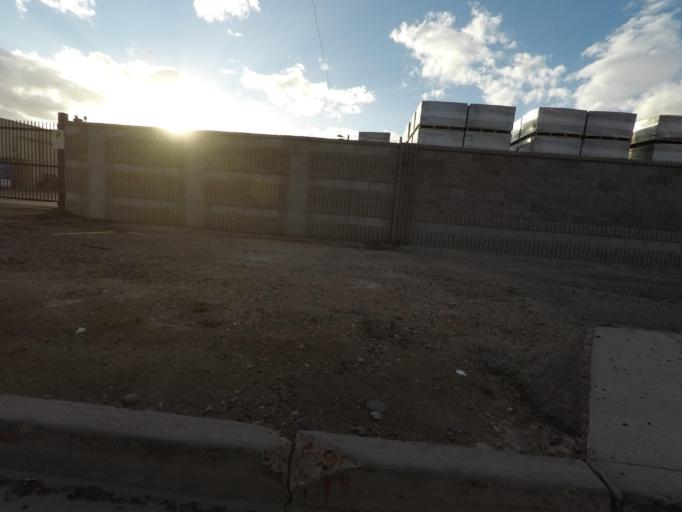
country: US
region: Arizona
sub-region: Maricopa County
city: Glendale
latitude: 33.5027
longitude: -112.1488
